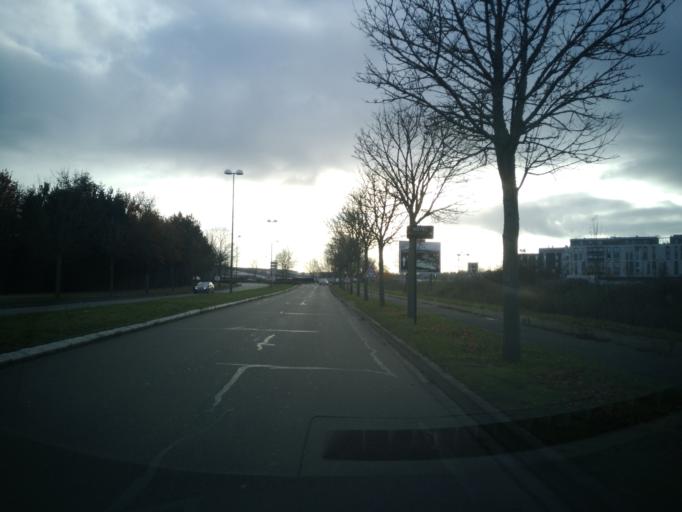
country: FR
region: Ile-de-France
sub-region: Departement des Yvelines
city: Guyancourt
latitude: 48.7674
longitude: 2.0809
